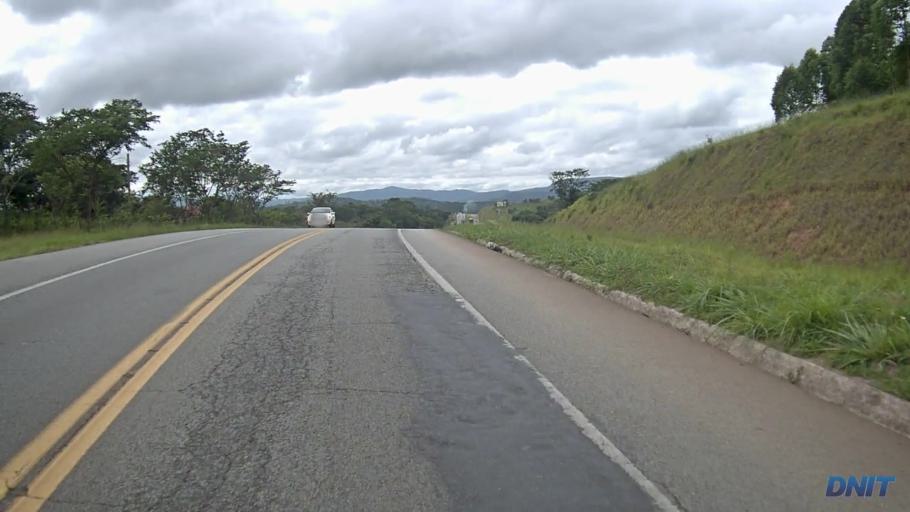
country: BR
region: Minas Gerais
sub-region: Barao De Cocais
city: Barao de Cocais
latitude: -19.7703
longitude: -43.4492
